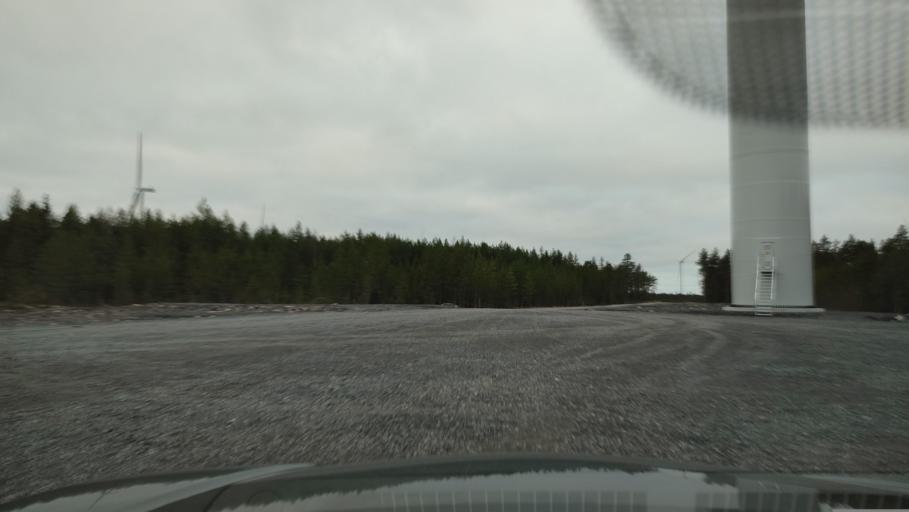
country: FI
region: Southern Ostrobothnia
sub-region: Suupohja
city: Karijoki
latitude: 62.1954
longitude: 21.5976
